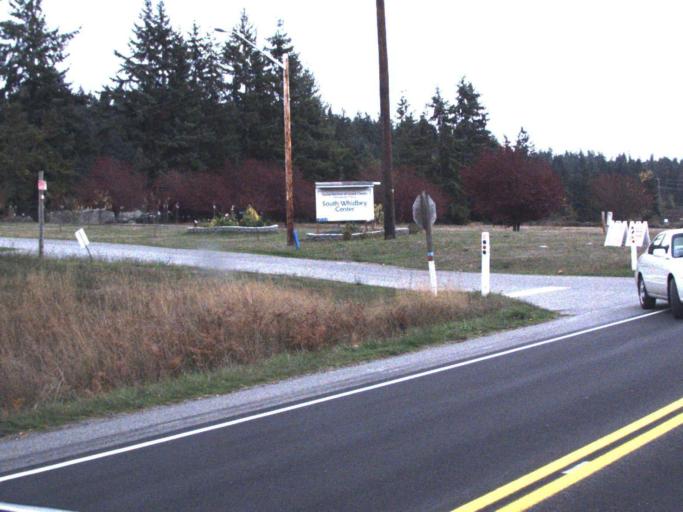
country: US
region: Washington
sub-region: Island County
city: Langley
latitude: 48.0026
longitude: -122.4604
